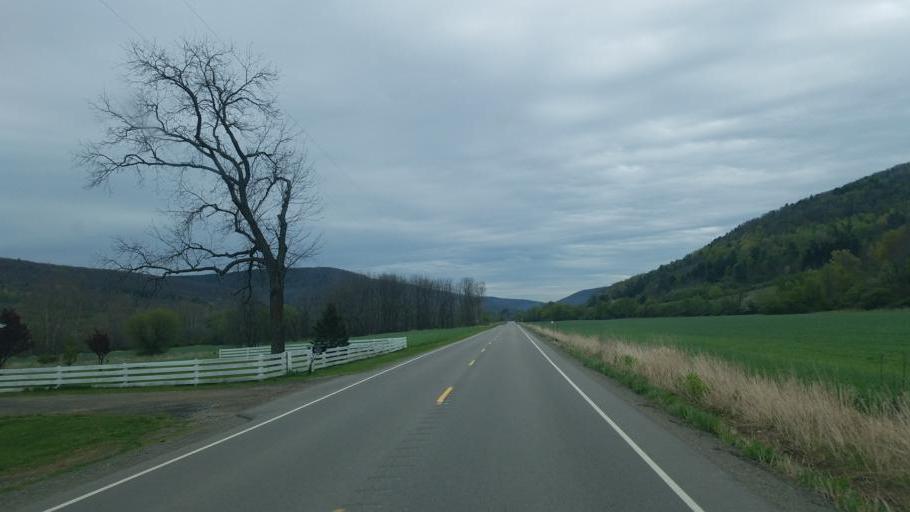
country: US
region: Pennsylvania
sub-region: Tioga County
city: Westfield
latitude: 41.9847
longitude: -77.4798
